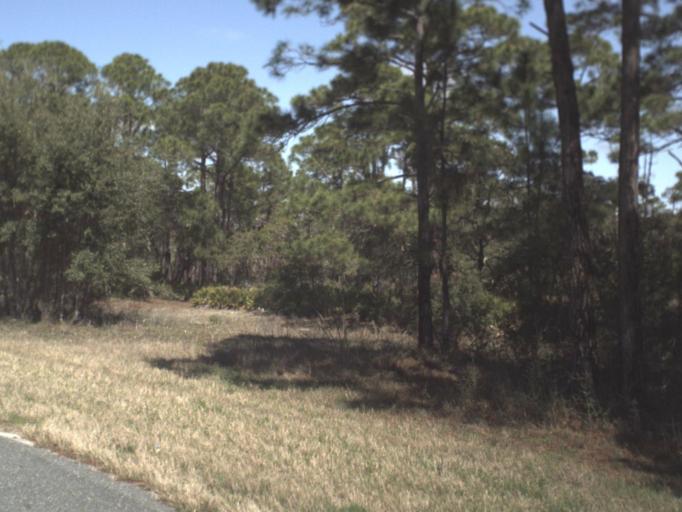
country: US
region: Florida
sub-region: Wakulla County
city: Crawfordville
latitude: 29.9847
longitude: -84.3857
